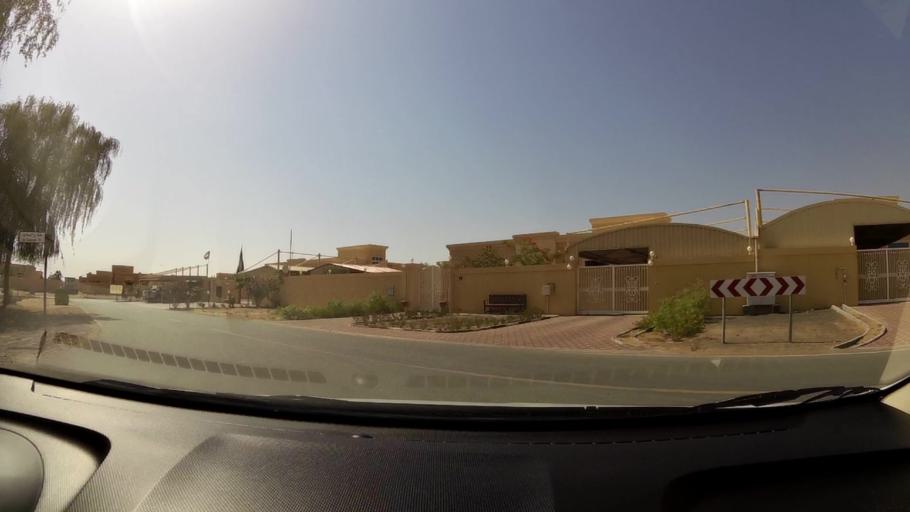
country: AE
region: Umm al Qaywayn
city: Umm al Qaywayn
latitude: 25.4768
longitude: 55.6154
